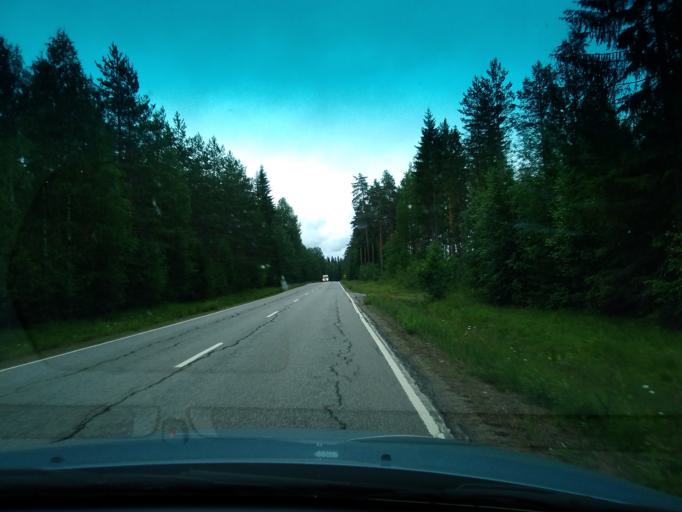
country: FI
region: Central Finland
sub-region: Keuruu
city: Multia
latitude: 62.4194
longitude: 24.7788
